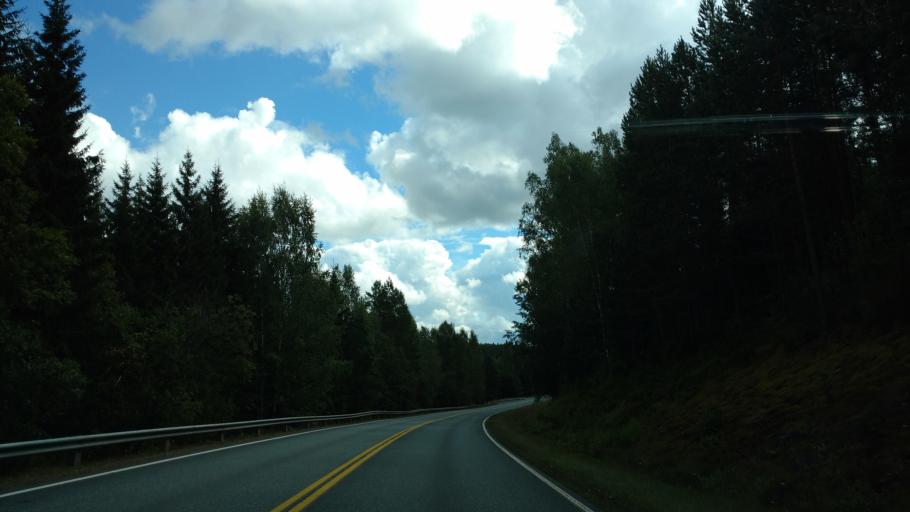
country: FI
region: Uusimaa
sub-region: Helsinki
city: Karjalohja
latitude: 60.2306
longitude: 23.6120
